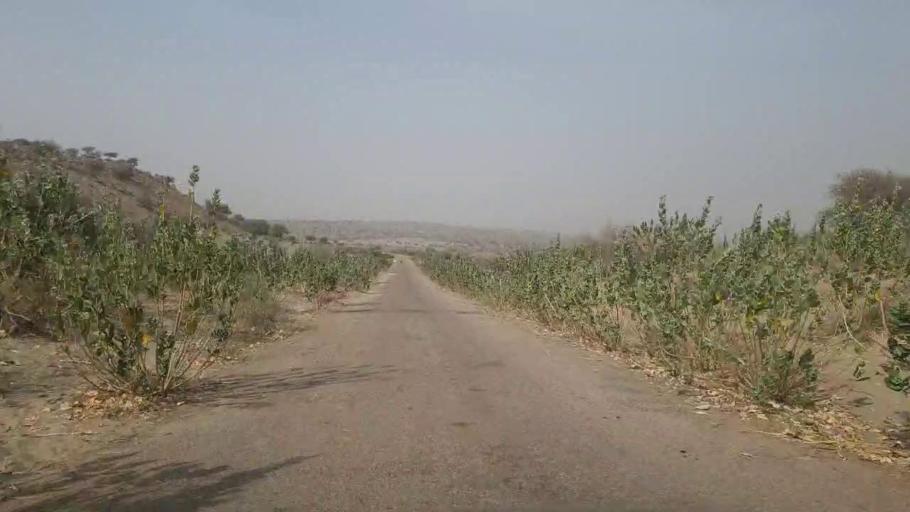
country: PK
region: Sindh
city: Chor
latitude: 25.6306
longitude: 69.9298
